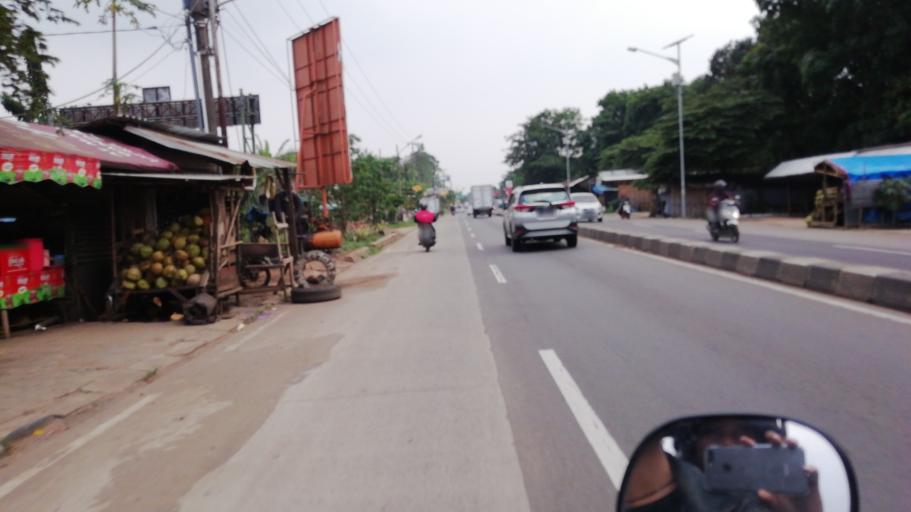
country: ID
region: West Java
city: Parung
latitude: -6.4905
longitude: 106.7396
